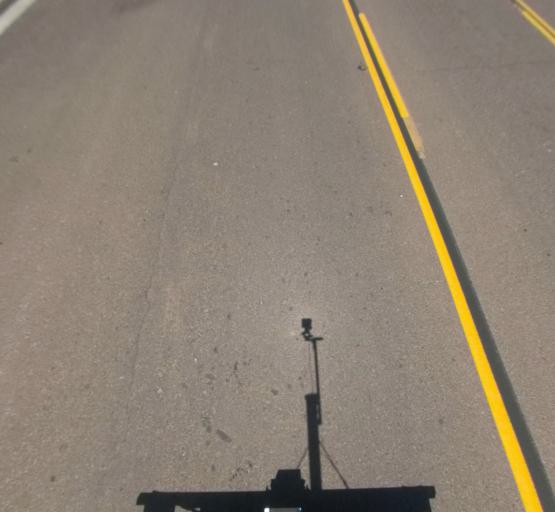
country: US
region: California
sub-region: Madera County
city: Madera
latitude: 36.9876
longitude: -120.0452
